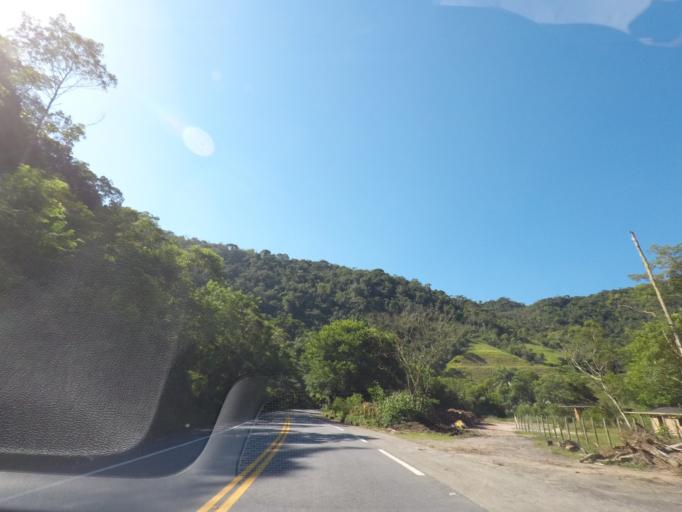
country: BR
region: Rio de Janeiro
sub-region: Parati
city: Paraty
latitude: -23.3398
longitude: -44.7372
